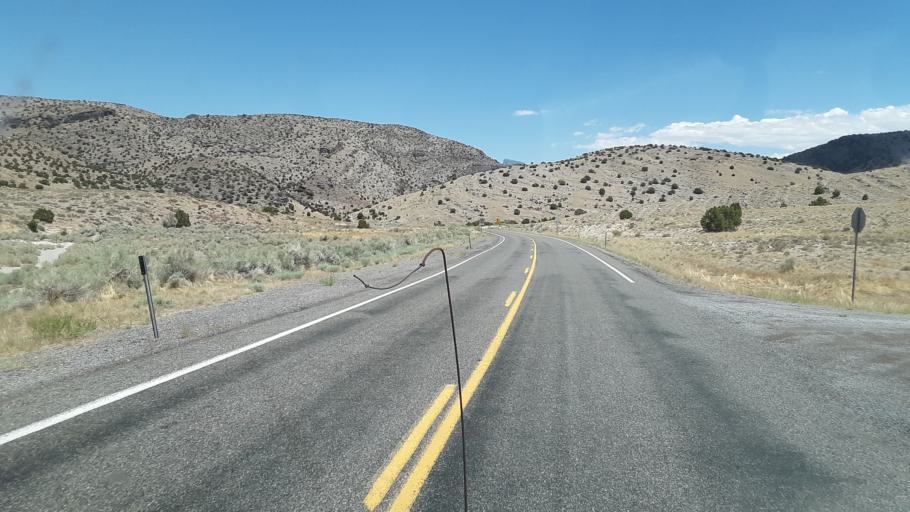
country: US
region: Utah
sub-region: Beaver County
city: Milford
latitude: 39.0787
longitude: -113.6093
